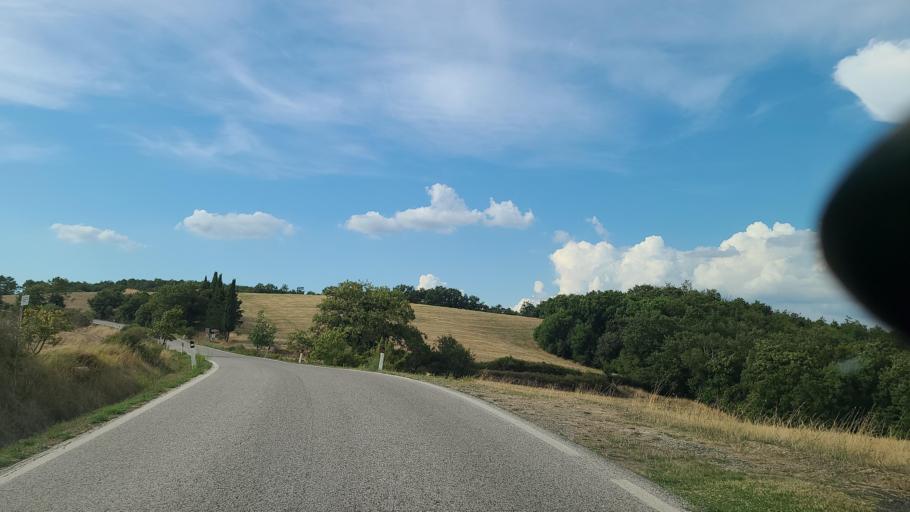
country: IT
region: Tuscany
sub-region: Provincia di Siena
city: San Gimignano
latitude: 43.4266
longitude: 10.9737
